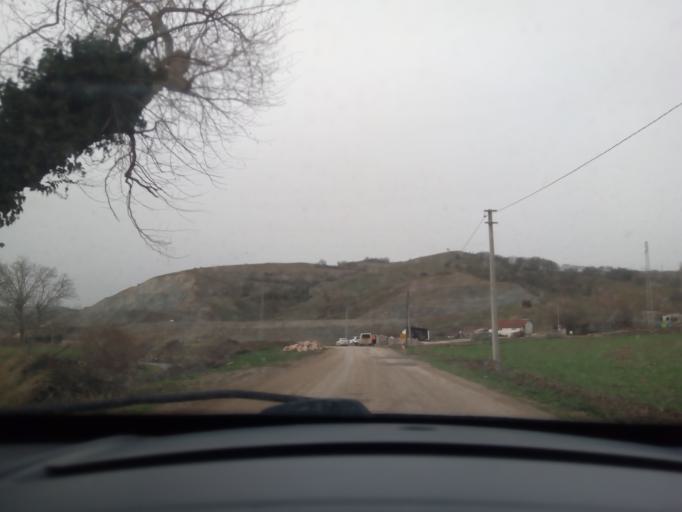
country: TR
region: Balikesir
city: Susurluk
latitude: 39.9182
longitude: 28.1321
